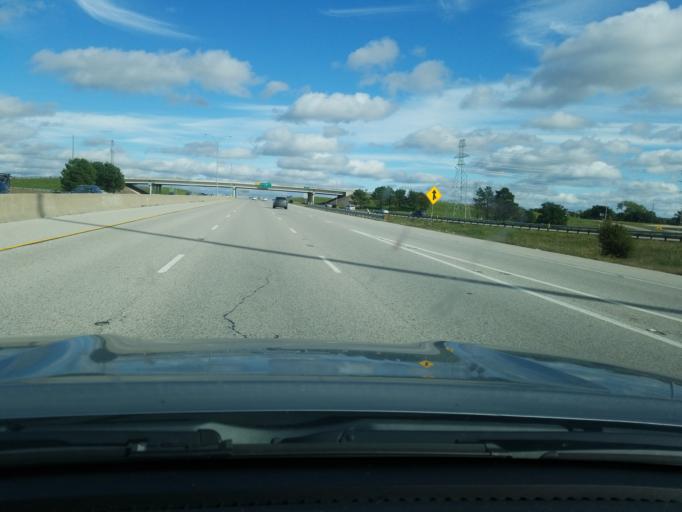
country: US
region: Texas
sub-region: Tarrant County
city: White Settlement
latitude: 32.7382
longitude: -97.4788
